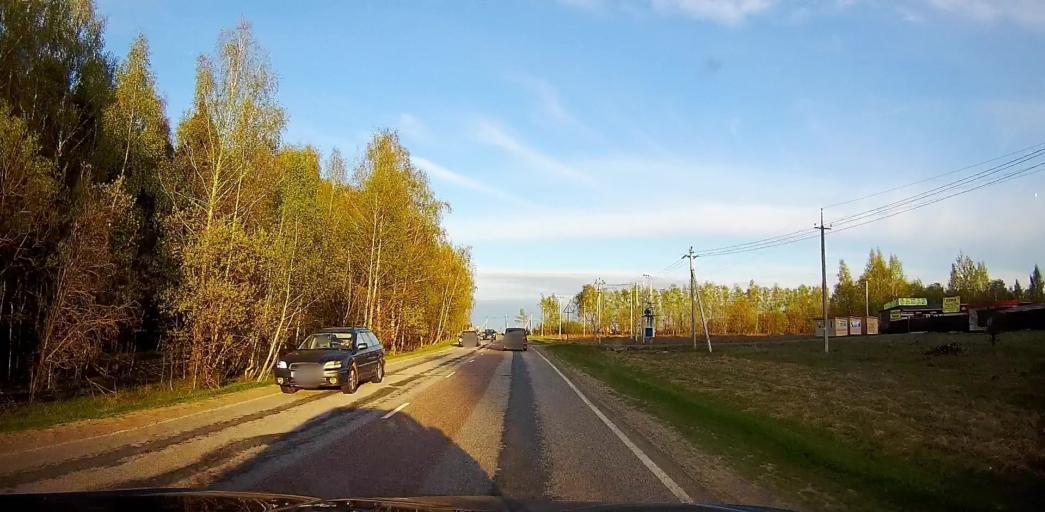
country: RU
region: Moskovskaya
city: Meshcherino
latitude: 55.2238
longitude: 38.3980
